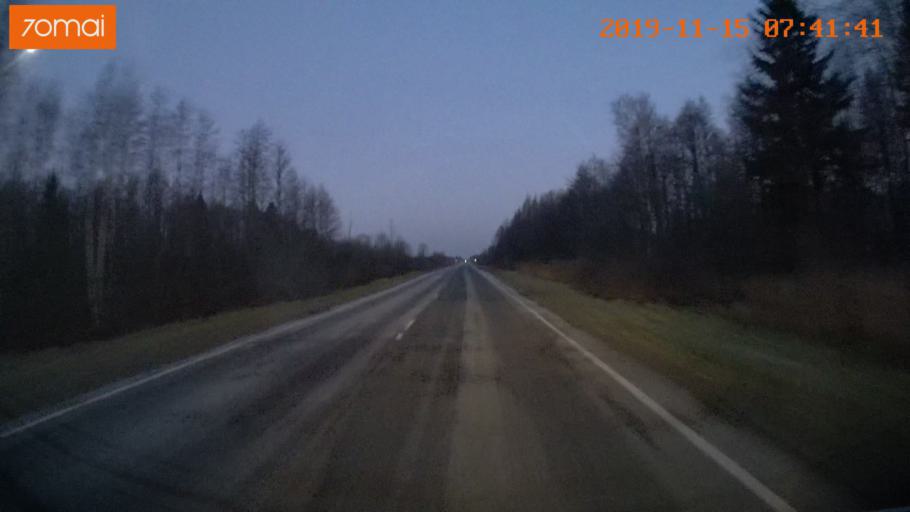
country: RU
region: Vologda
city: Sheksna
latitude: 58.7853
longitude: 38.3515
